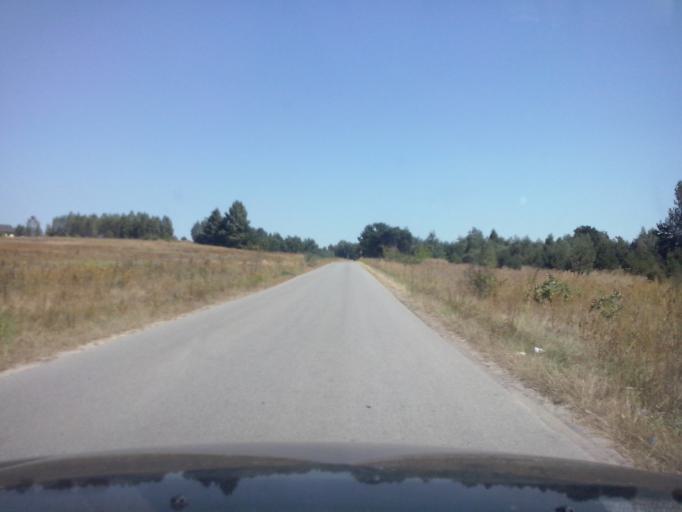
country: PL
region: Swietokrzyskie
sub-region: Powiat kielecki
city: Bieliny
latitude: 50.8242
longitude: 20.9054
